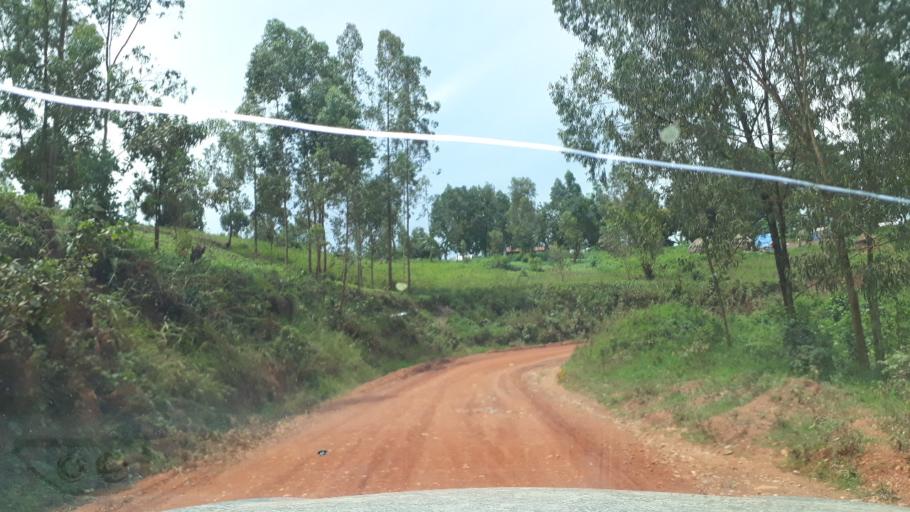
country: CD
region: Eastern Province
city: Bunia
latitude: 1.7263
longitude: 30.3160
